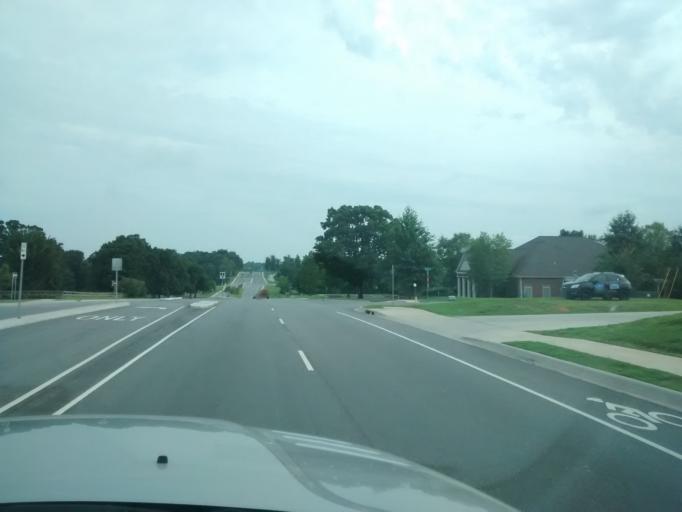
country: US
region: Arkansas
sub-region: Washington County
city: Johnson
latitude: 36.1313
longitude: -94.1178
